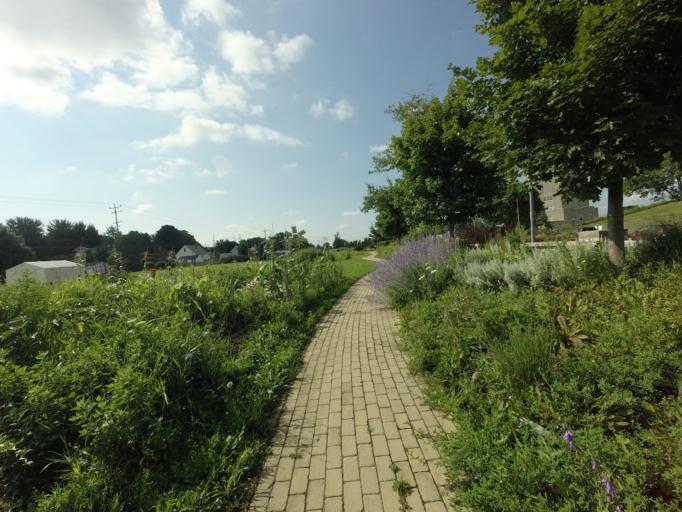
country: US
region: Wisconsin
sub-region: Milwaukee County
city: Saint Francis
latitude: 42.9731
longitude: -87.9192
